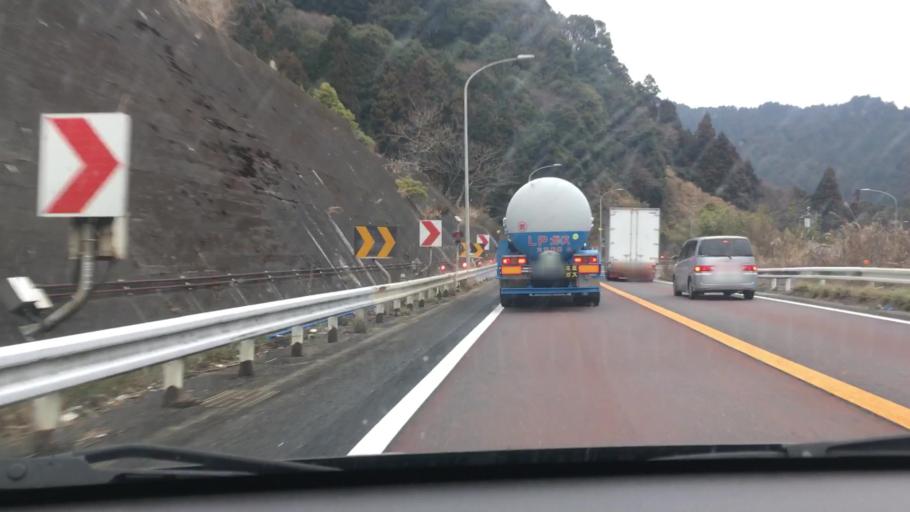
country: JP
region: Mie
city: Kameyama
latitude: 34.8399
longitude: 136.3605
